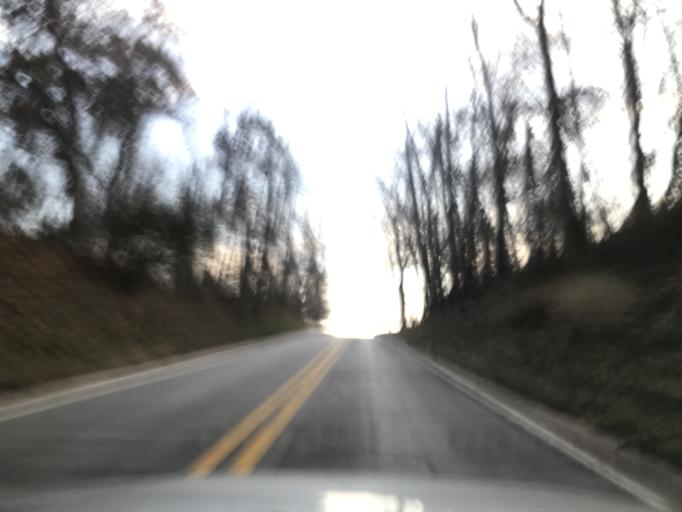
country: US
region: Illinois
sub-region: Henderson County
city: Oquawka
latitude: 40.9988
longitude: -90.8537
